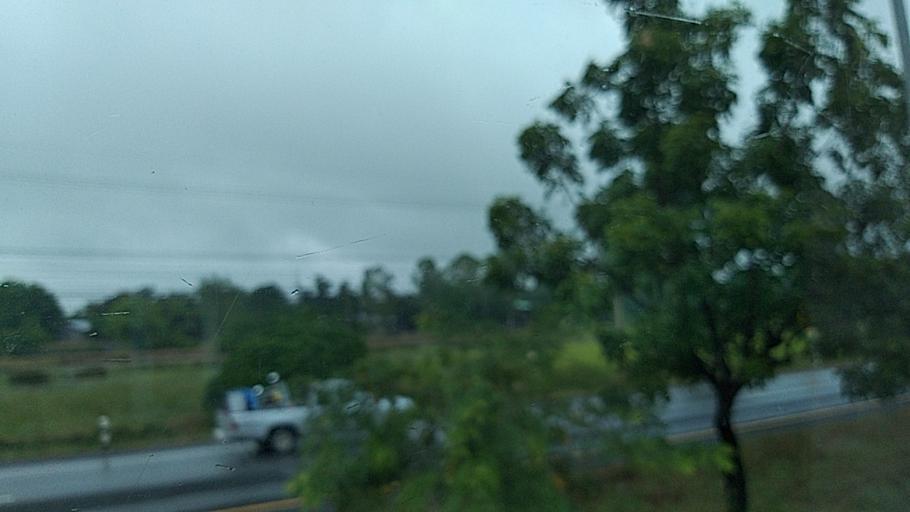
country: TH
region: Nakhon Ratchasima
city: Non Sung
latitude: 15.1873
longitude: 102.3433
